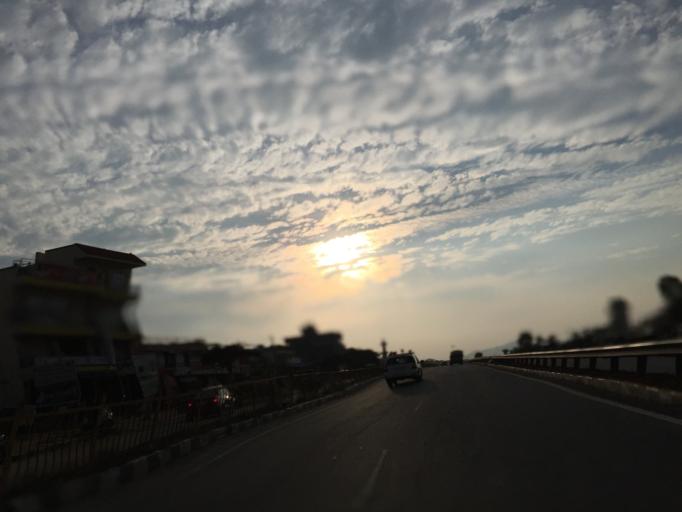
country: IN
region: Karnataka
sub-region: Kolar
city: Kolar
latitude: 13.1321
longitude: 78.1649
